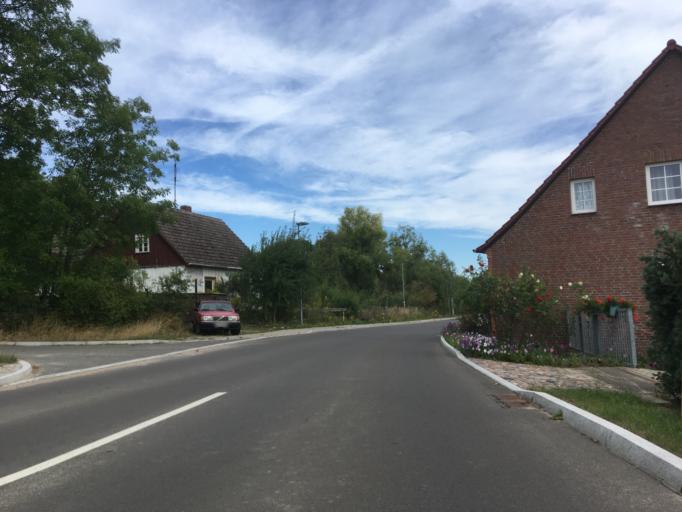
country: DE
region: Brandenburg
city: Mittenwalde
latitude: 53.2250
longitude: 13.5793
